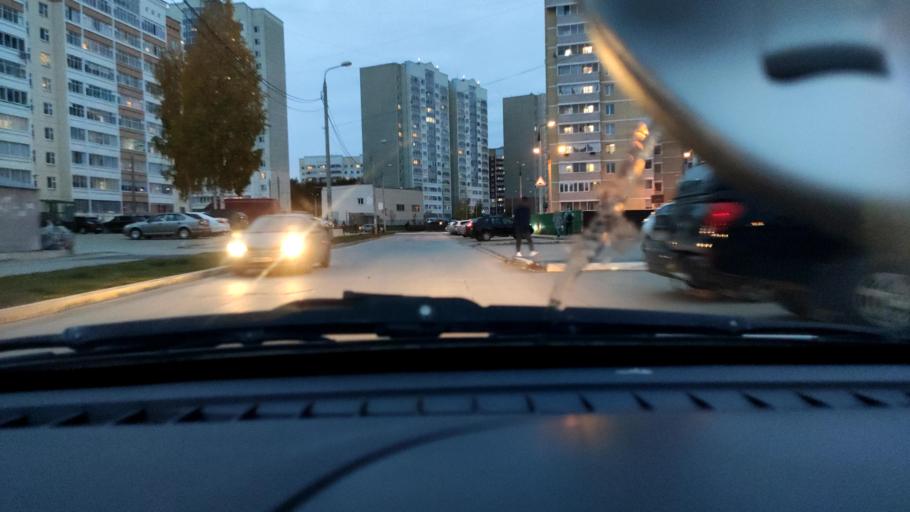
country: RU
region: Perm
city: Kondratovo
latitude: 58.0328
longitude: 56.1397
